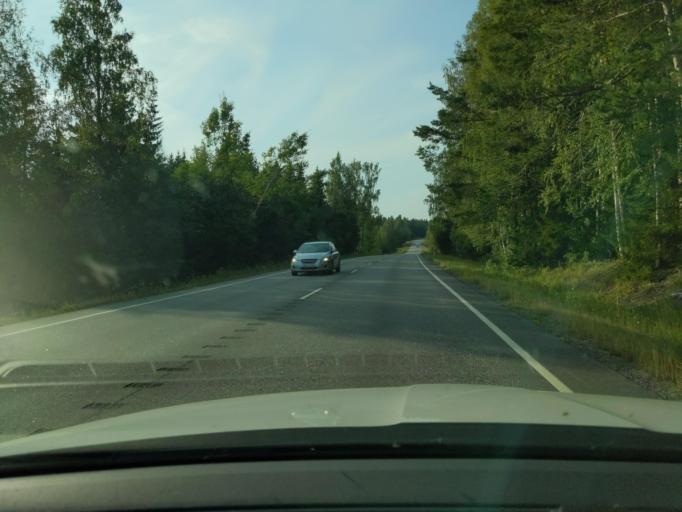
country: FI
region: Paijanne Tavastia
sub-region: Lahti
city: Padasjoki
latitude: 61.3211
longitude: 25.2811
